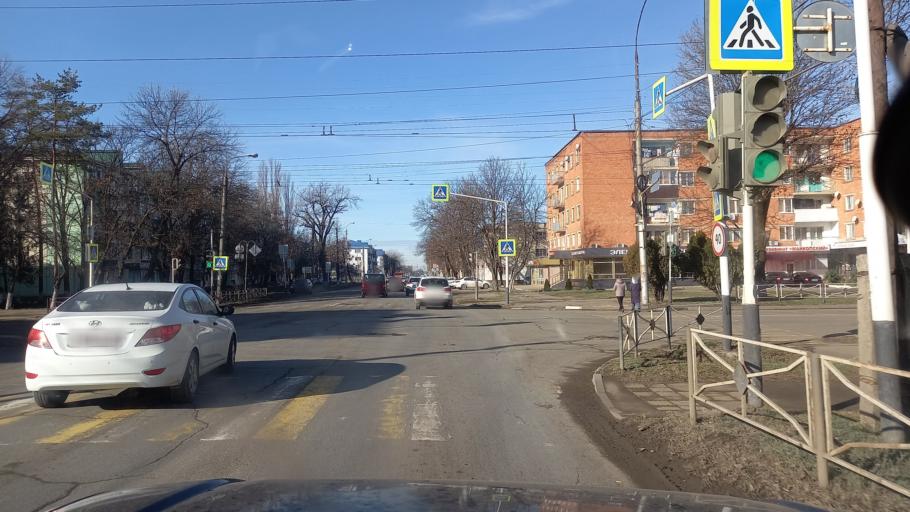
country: RU
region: Adygeya
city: Maykop
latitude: 44.6172
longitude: 40.1096
